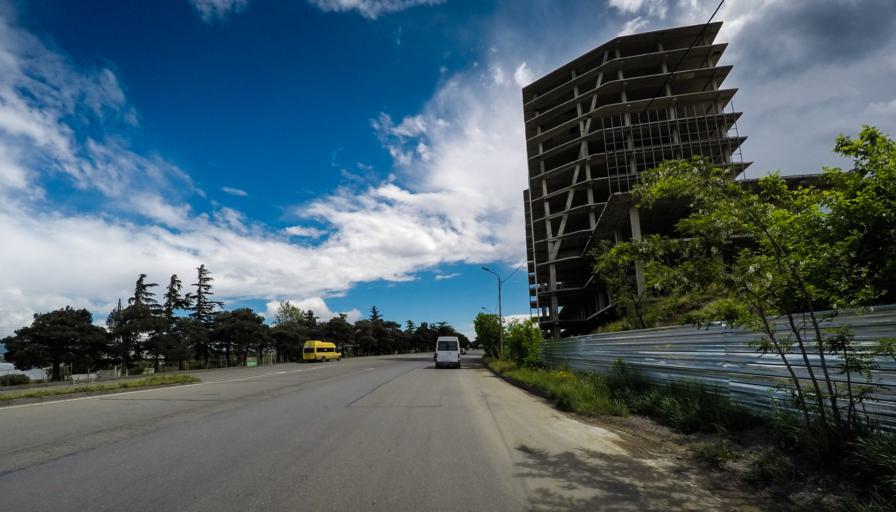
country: GE
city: Zahesi
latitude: 41.8227
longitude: 44.7690
